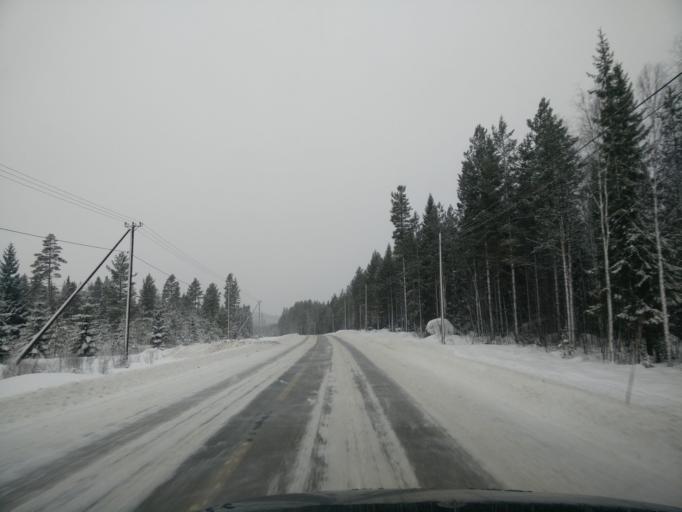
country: SE
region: Jaemtland
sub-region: Braecke Kommun
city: Braecke
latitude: 62.3972
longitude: 15.1694
